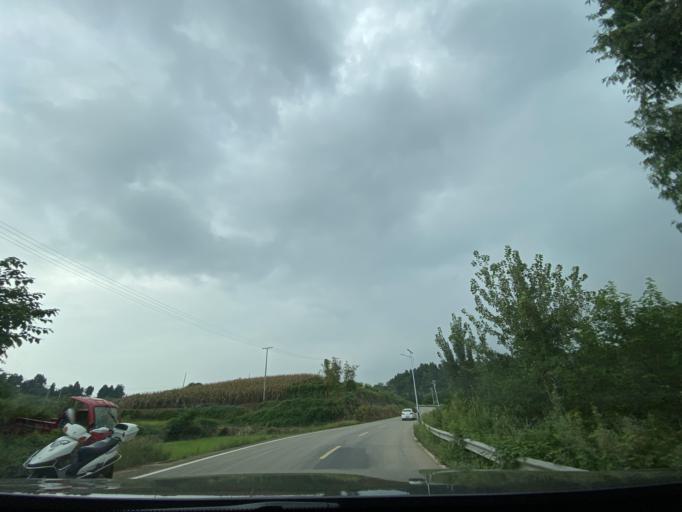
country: CN
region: Sichuan
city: Jiancheng
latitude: 30.5504
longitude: 104.5235
